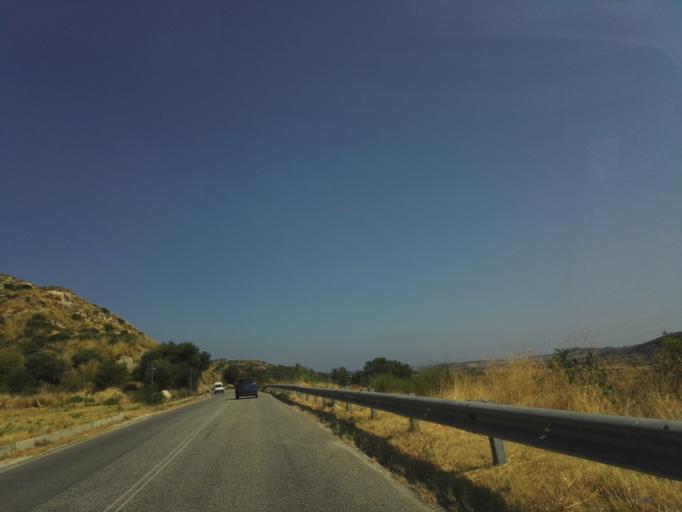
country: IT
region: Calabria
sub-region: Provincia di Reggio Calabria
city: Monasterace
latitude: 38.4643
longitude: 16.5136
